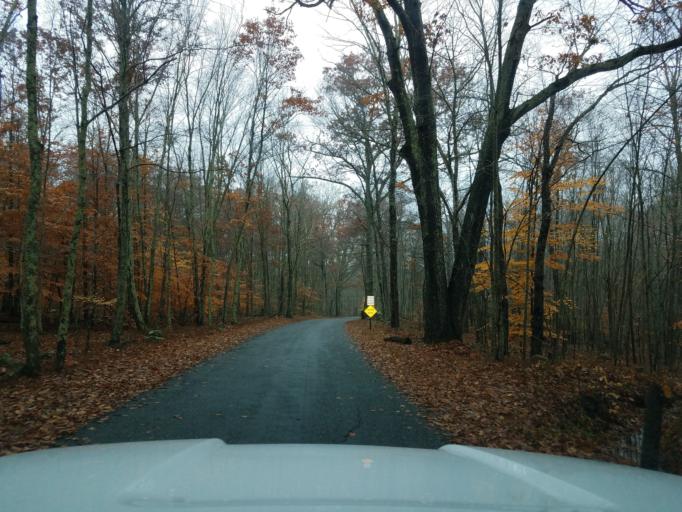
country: US
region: Connecticut
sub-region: Windham County
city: Windham
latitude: 41.7979
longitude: -72.1093
